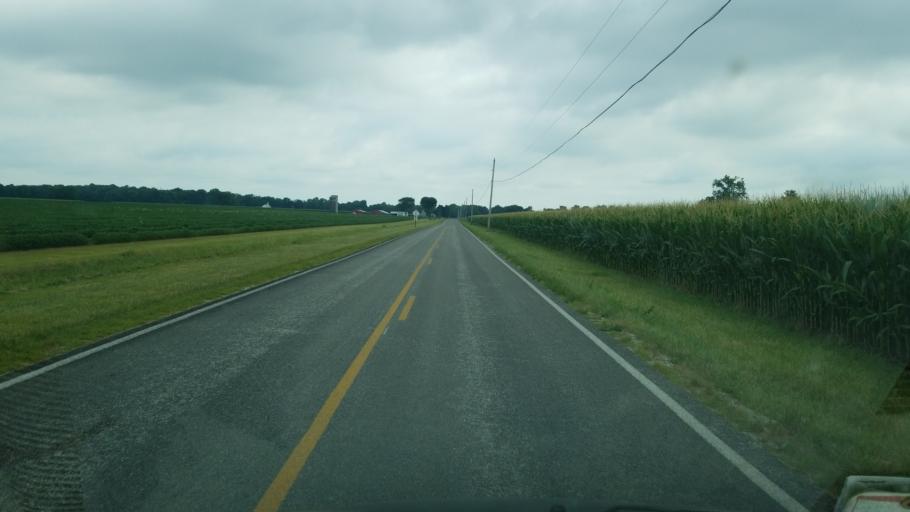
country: US
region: Ohio
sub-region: Sandusky County
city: Green Springs
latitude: 41.2147
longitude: -83.1387
